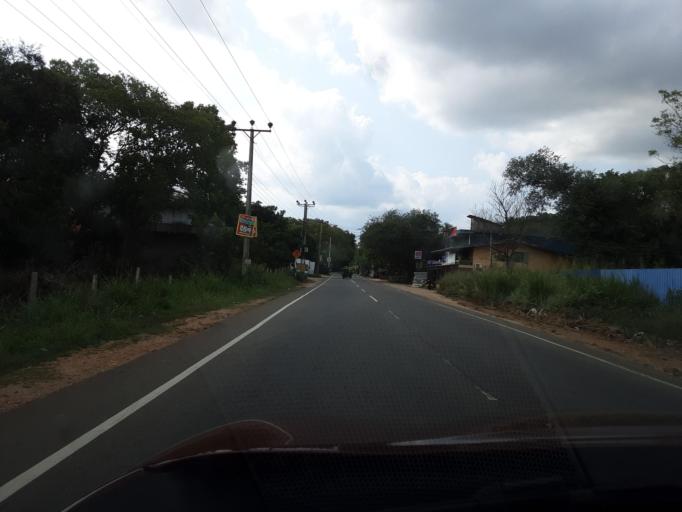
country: LK
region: Uva
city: Haputale
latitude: 6.5212
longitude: 81.1255
